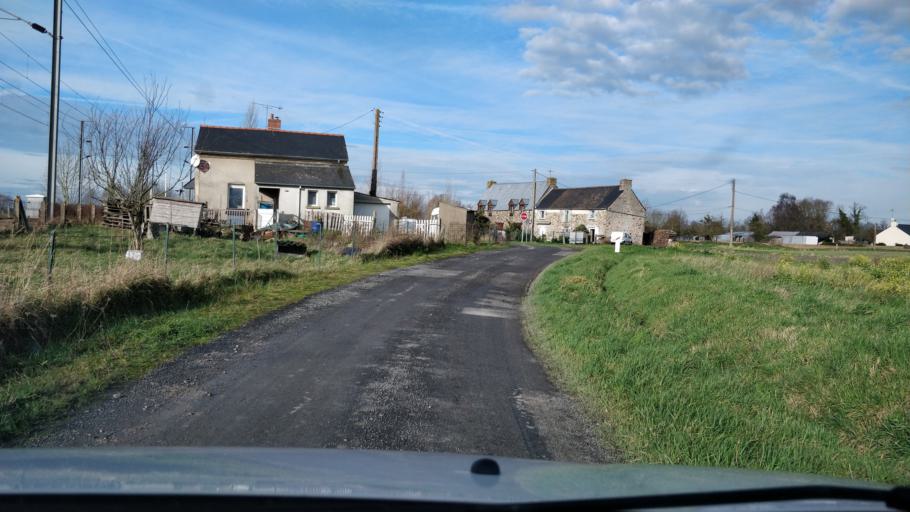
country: FR
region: Brittany
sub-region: Departement d'Ille-et-Vilaine
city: Hirel
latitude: 48.5815
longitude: -1.8145
